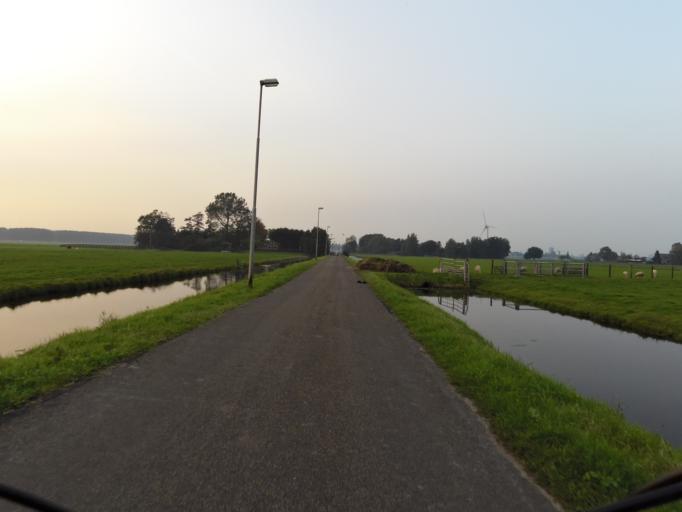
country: NL
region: South Holland
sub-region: Gemeente Leiden
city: Leiden
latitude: 52.1168
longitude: 4.4893
